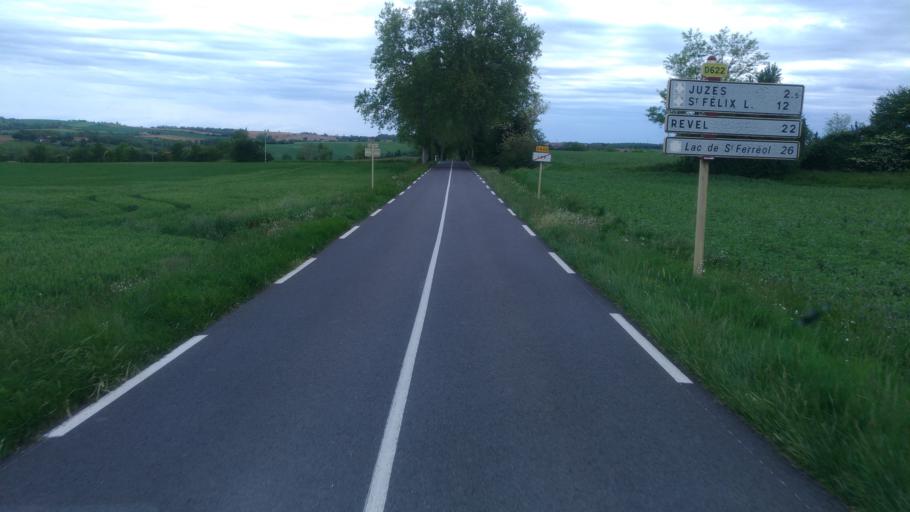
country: FR
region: Midi-Pyrenees
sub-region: Departement de la Haute-Garonne
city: Avignonet-Lauragais
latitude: 43.4375
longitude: 1.7804
